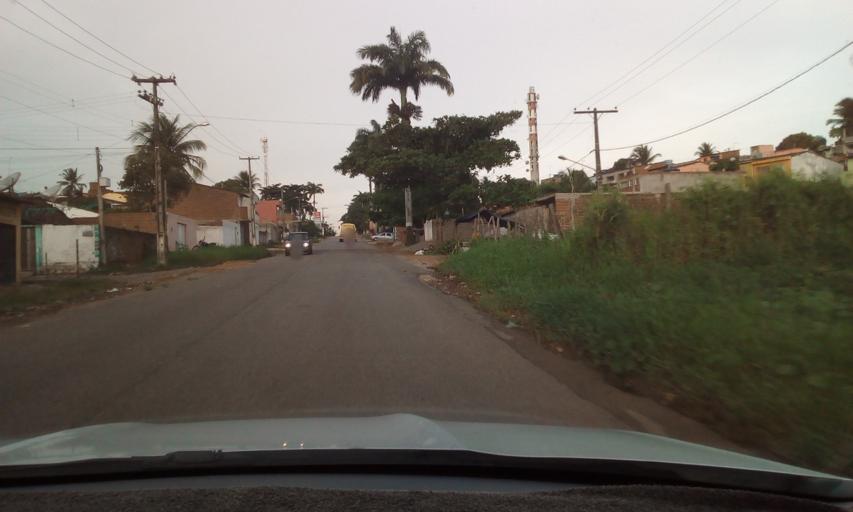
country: BR
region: Pernambuco
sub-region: Vicencia
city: Vicencia
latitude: -7.5999
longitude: -35.2355
